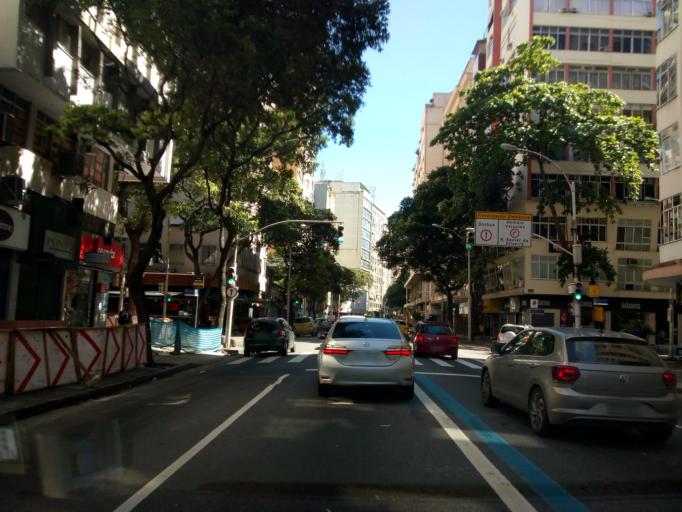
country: BR
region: Rio de Janeiro
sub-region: Rio De Janeiro
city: Rio de Janeiro
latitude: -22.9773
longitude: -43.1905
